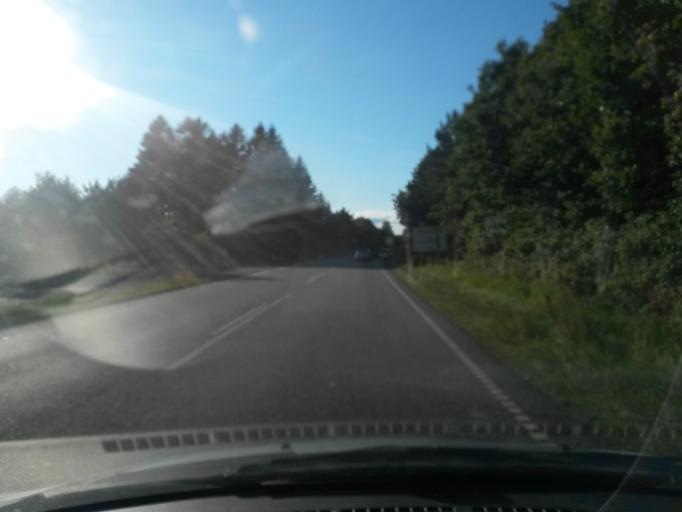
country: DK
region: Central Jutland
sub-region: Viborg Kommune
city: Bjerringbro
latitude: 56.3040
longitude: 9.6134
